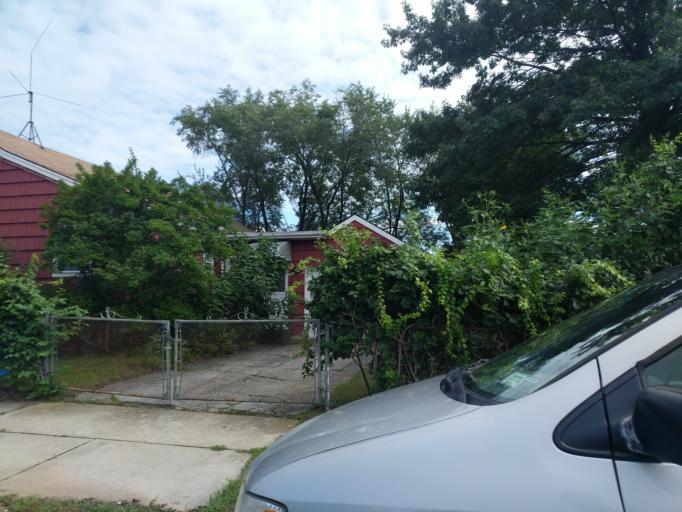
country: US
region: New York
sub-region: Nassau County
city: Cedarhurst
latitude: 40.6297
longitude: -73.7282
